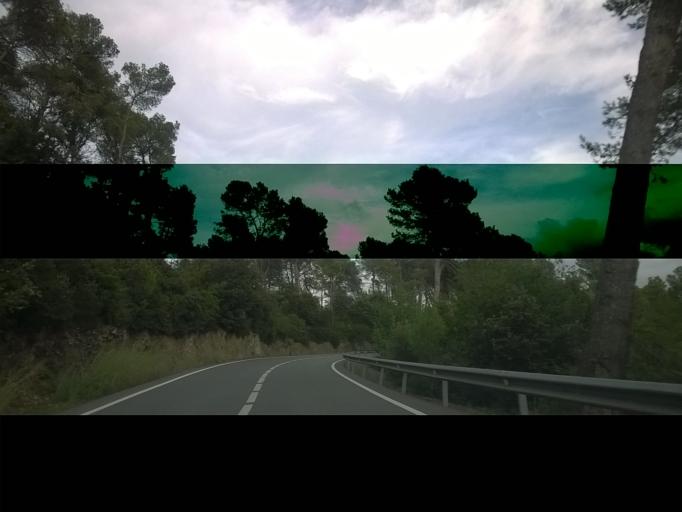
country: ES
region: Catalonia
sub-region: Provincia de Barcelona
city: Sant Cugat del Valles
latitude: 41.4429
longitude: 2.0976
